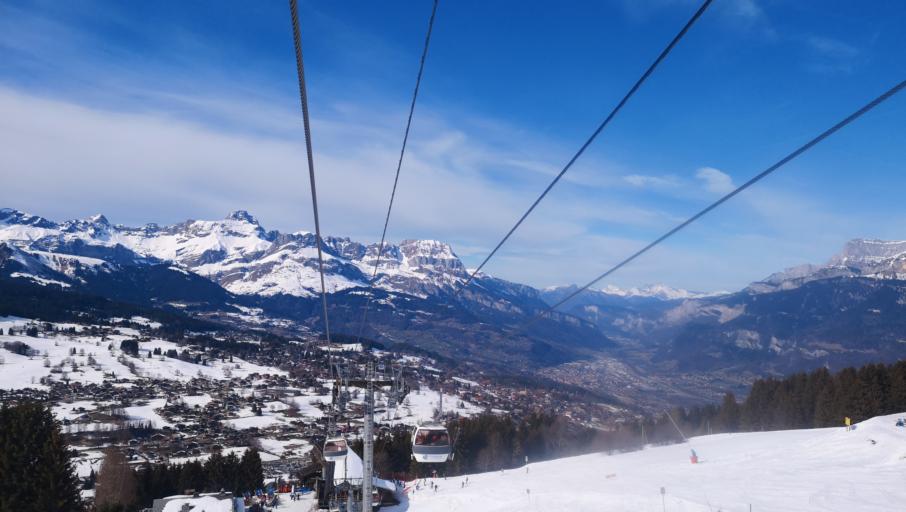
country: FR
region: Rhone-Alpes
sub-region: Departement de la Haute-Savoie
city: Combloux
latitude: 45.8710
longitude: 6.6520
